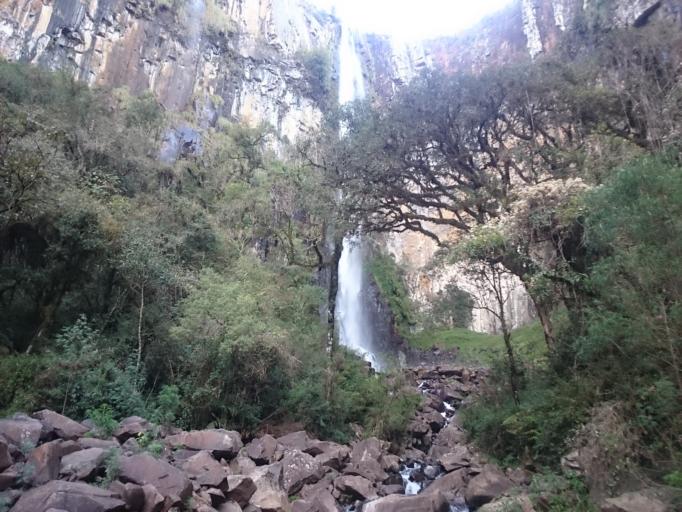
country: BR
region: Santa Catarina
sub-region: Sao Joaquim
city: Sao Joaquim
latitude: -28.0461
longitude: -49.6171
